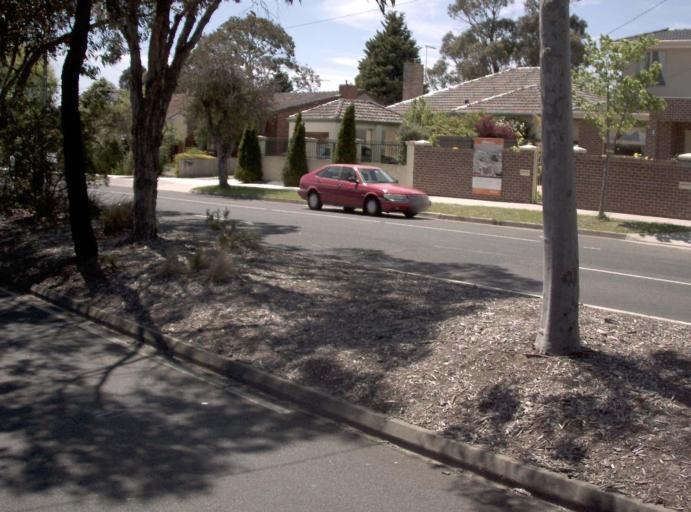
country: AU
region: Victoria
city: Burwood East
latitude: -37.8557
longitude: 145.1513
